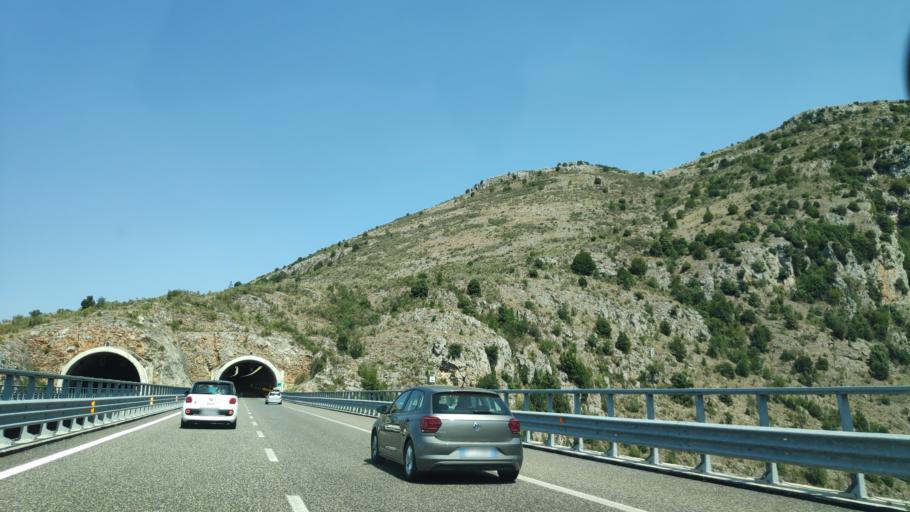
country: IT
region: Basilicate
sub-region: Provincia di Potenza
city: Lauria
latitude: 40.0365
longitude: 15.8735
